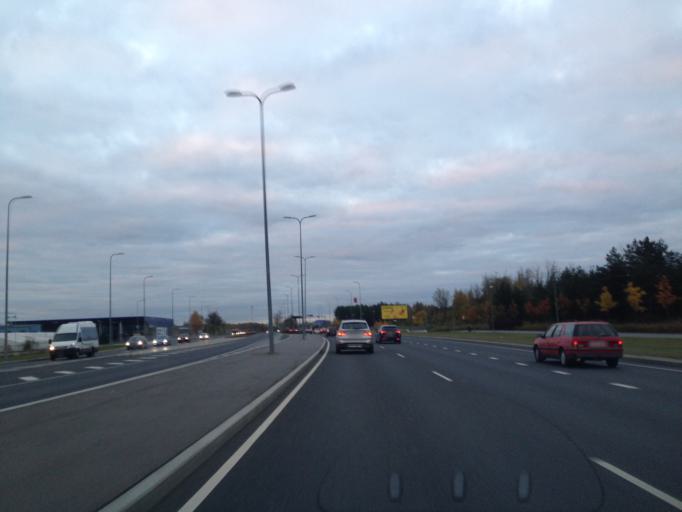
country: EE
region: Harju
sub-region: Tallinna linn
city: Tallinn
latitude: 59.4118
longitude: 24.7570
